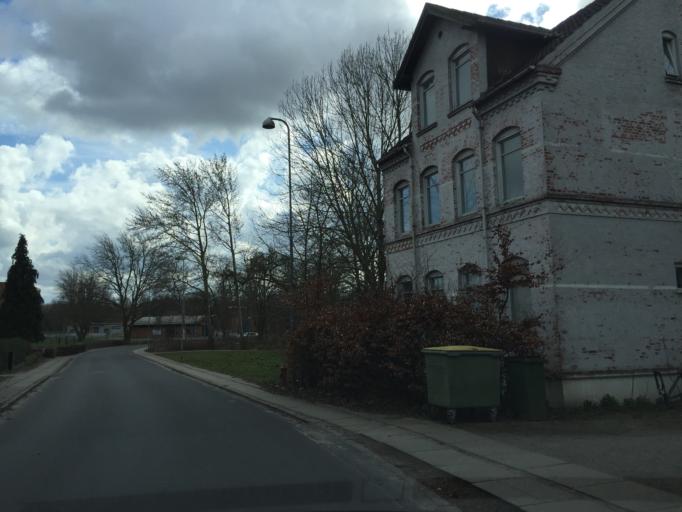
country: DK
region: South Denmark
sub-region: Odense Kommune
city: Odense
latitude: 55.3984
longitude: 10.4139
